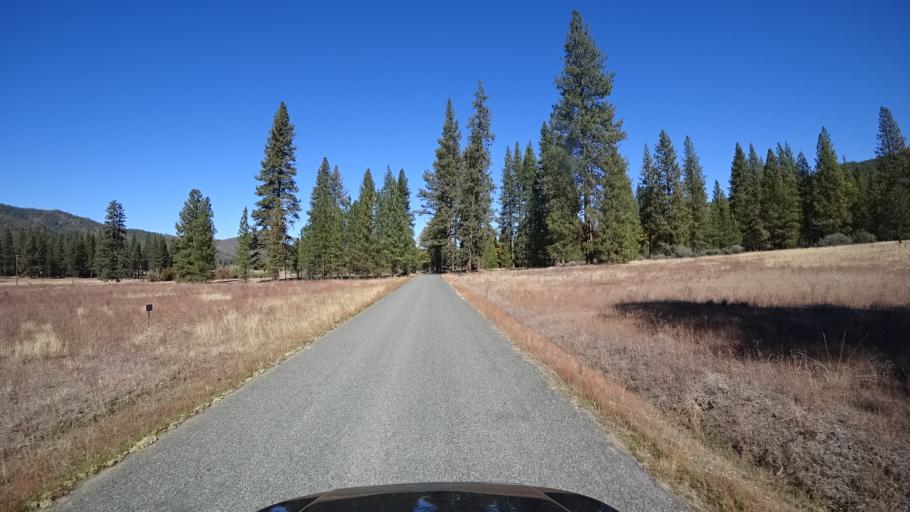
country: US
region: California
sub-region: Siskiyou County
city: Yreka
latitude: 41.5860
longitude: -122.9051
